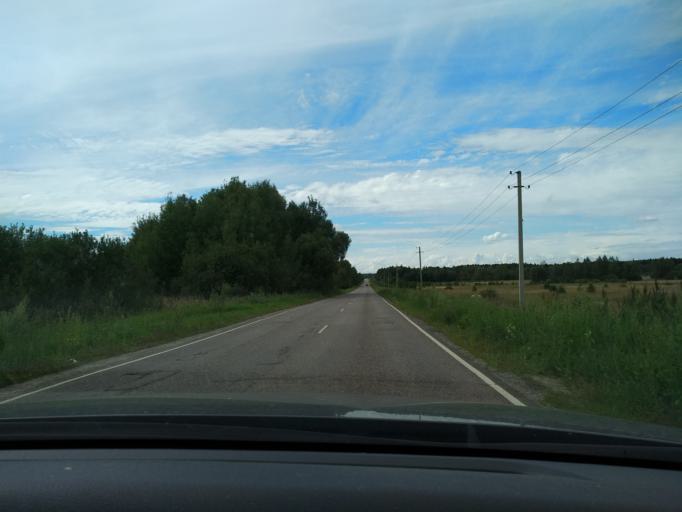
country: RU
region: Moskovskaya
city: Krasnyy Tkach
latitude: 55.3852
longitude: 39.1812
